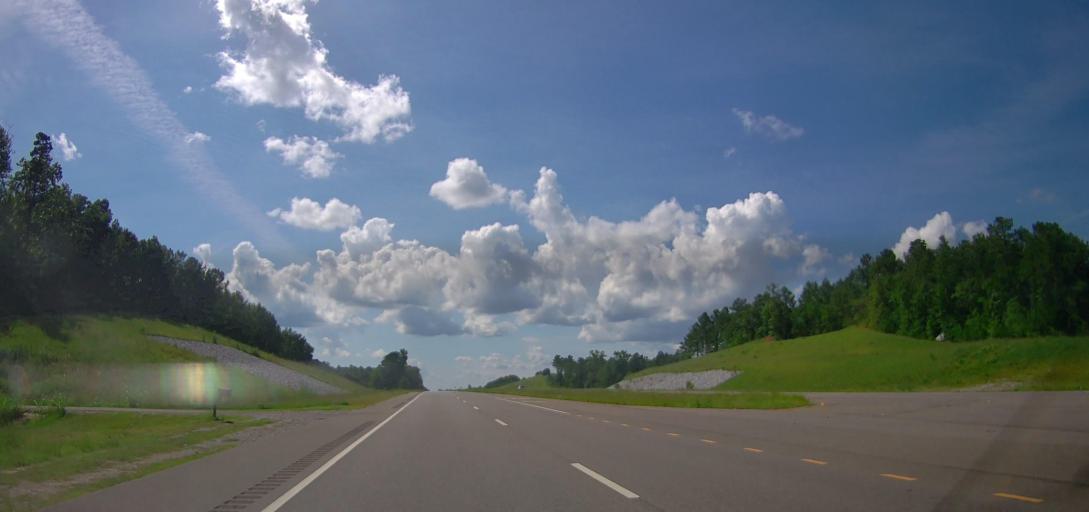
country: US
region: Alabama
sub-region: Pickens County
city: Reform
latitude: 33.3572
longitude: -87.9687
